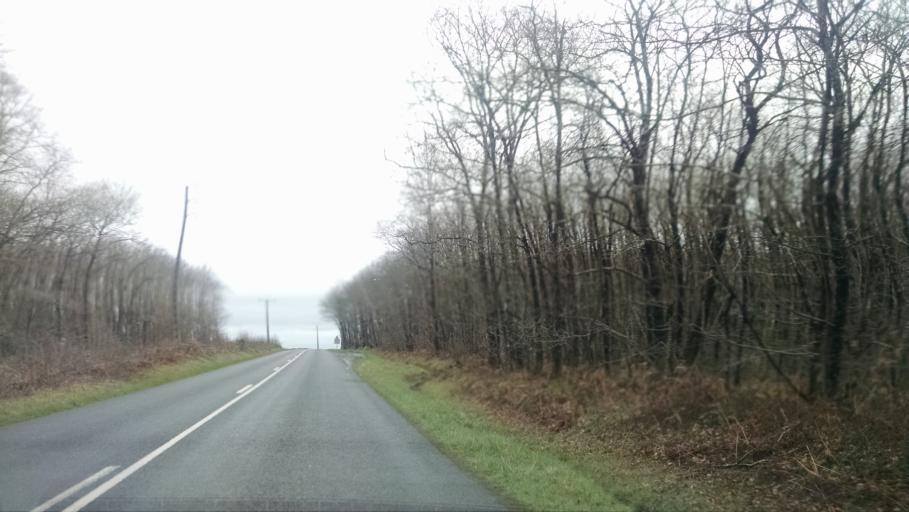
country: FR
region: Pays de la Loire
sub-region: Departement de la Loire-Atlantique
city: Monnieres
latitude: 47.1222
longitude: -1.3623
